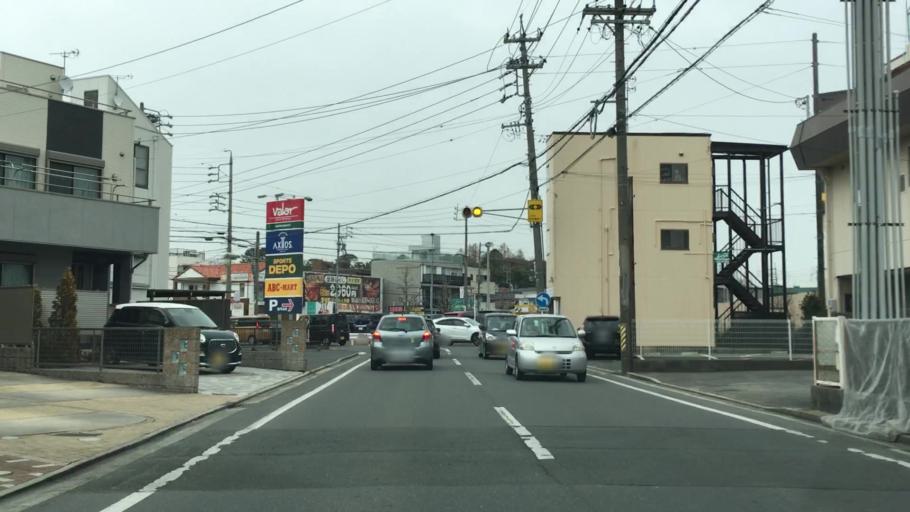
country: JP
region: Aichi
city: Toyohashi
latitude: 34.7548
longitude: 137.3923
